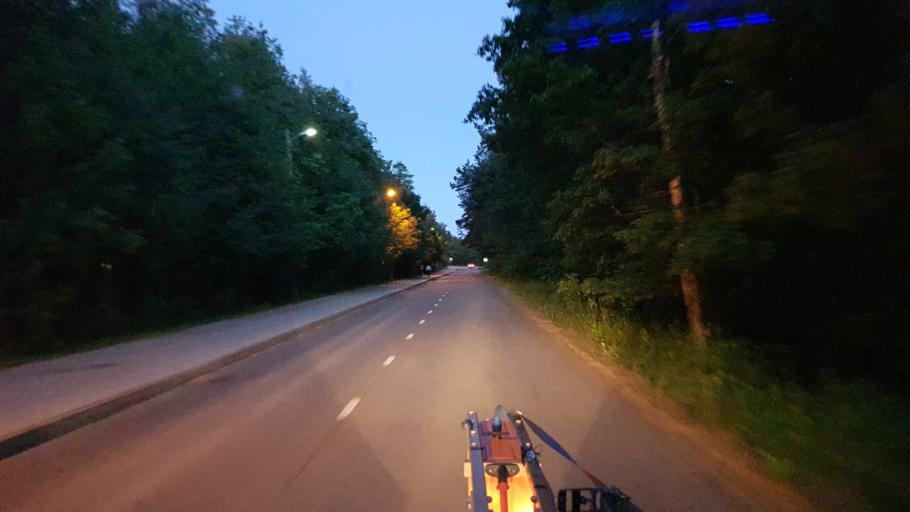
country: EE
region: Harju
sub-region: Harku vald
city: Tabasalu
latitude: 59.4482
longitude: 24.5909
